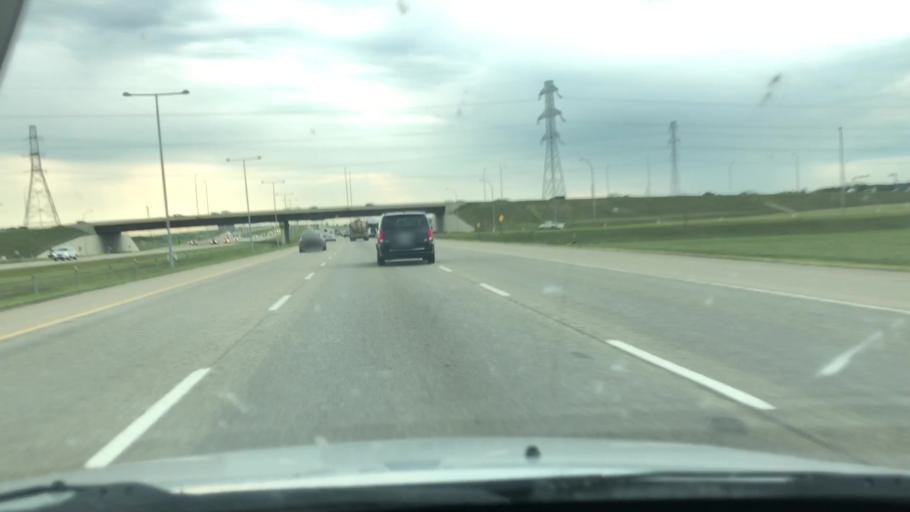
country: CA
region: Alberta
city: Beaumont
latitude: 53.4374
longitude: -113.4623
